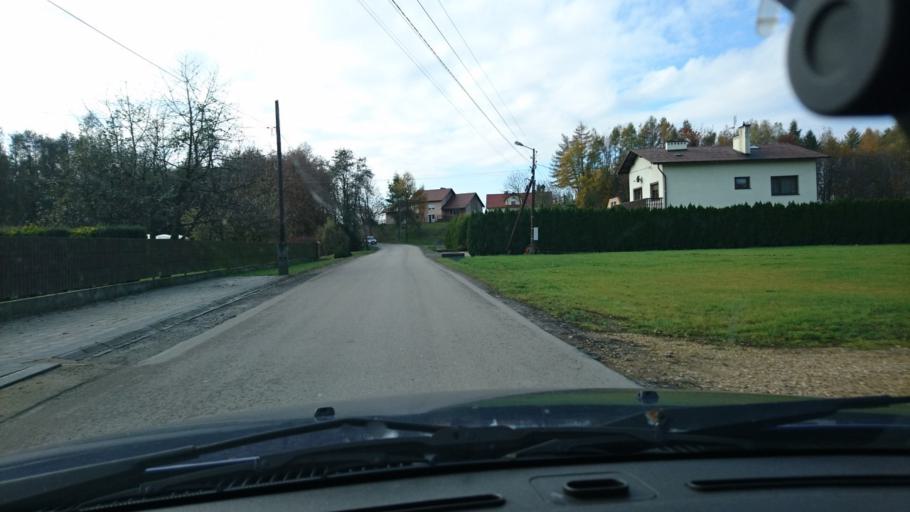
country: PL
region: Silesian Voivodeship
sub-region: Powiat bielski
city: Wilamowice
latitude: 49.9321
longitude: 19.1815
